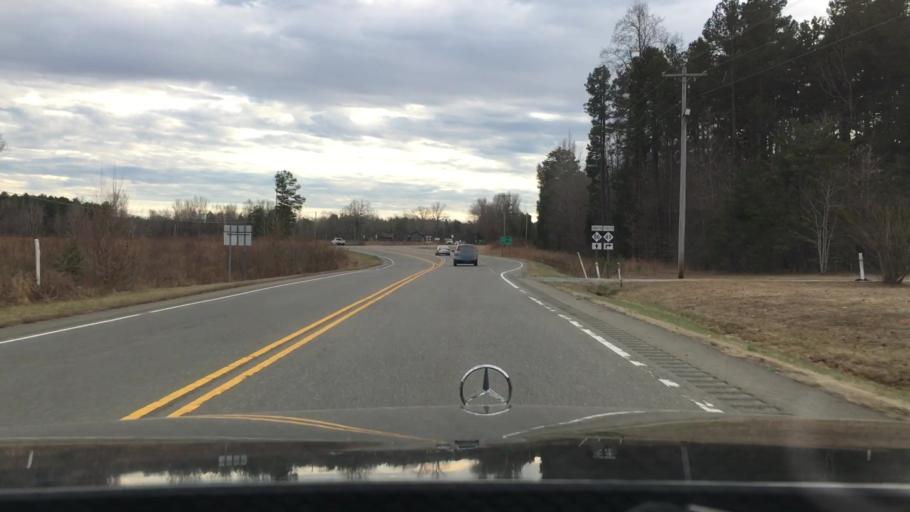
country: US
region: North Carolina
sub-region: Alamance County
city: Mebane
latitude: 36.2415
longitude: -79.1903
